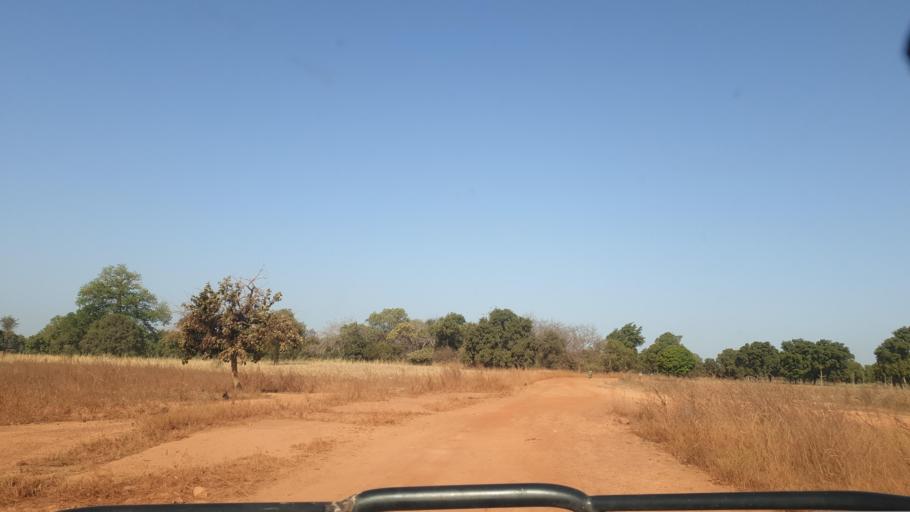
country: ML
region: Sikasso
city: Kolondieba
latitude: 11.7342
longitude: -6.8920
